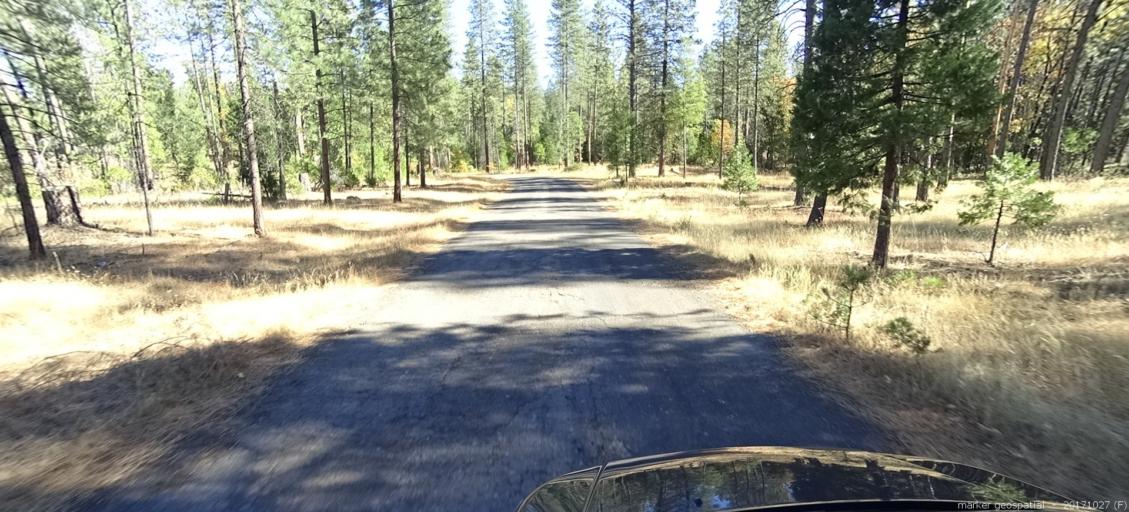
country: US
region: California
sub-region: Shasta County
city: Shingletown
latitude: 40.6214
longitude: -121.8405
